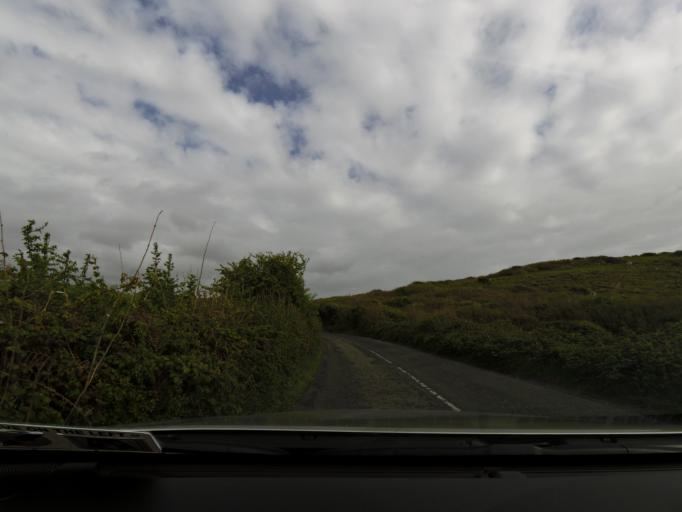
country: IE
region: Connaught
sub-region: County Galway
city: Bearna
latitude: 53.0559
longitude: -9.3541
